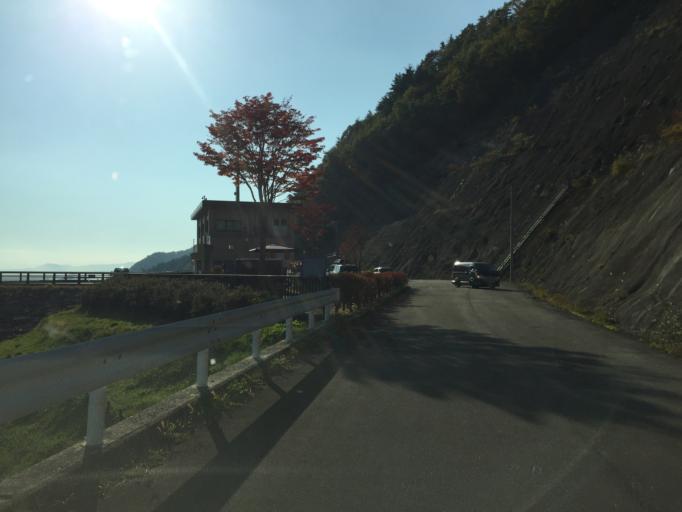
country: JP
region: Fukushima
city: Kitakata
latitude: 37.7546
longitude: 139.9073
